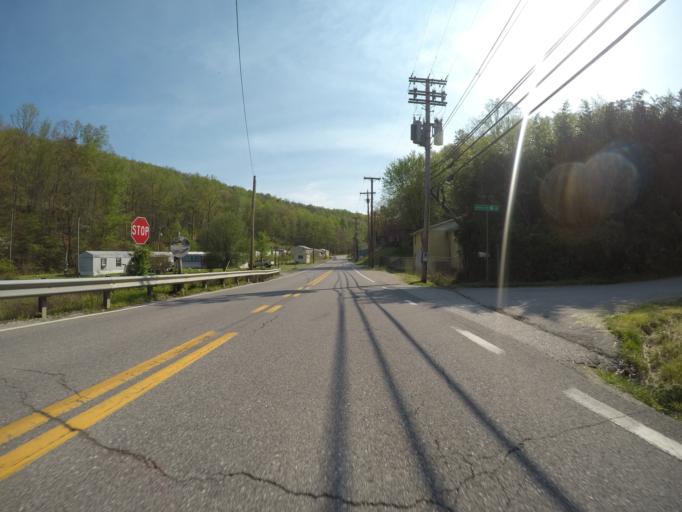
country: US
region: West Virginia
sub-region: Kanawha County
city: Coal Fork
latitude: 38.3815
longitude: -81.5617
